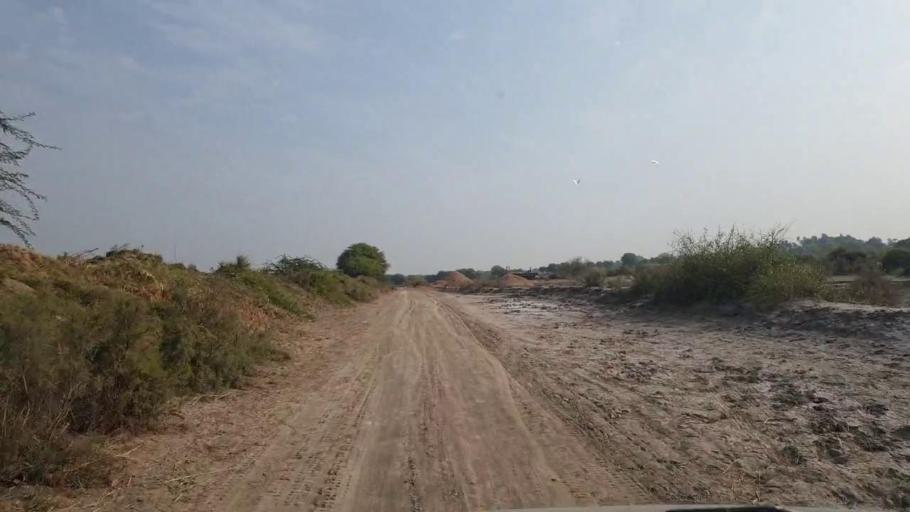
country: PK
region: Sindh
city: Talhar
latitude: 24.9036
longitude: 68.8960
